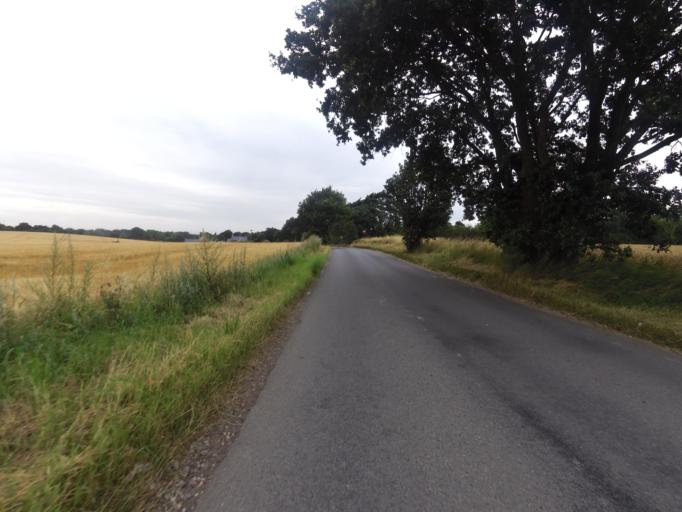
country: GB
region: England
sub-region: Suffolk
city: Ipswich
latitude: 52.0825
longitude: 1.1805
